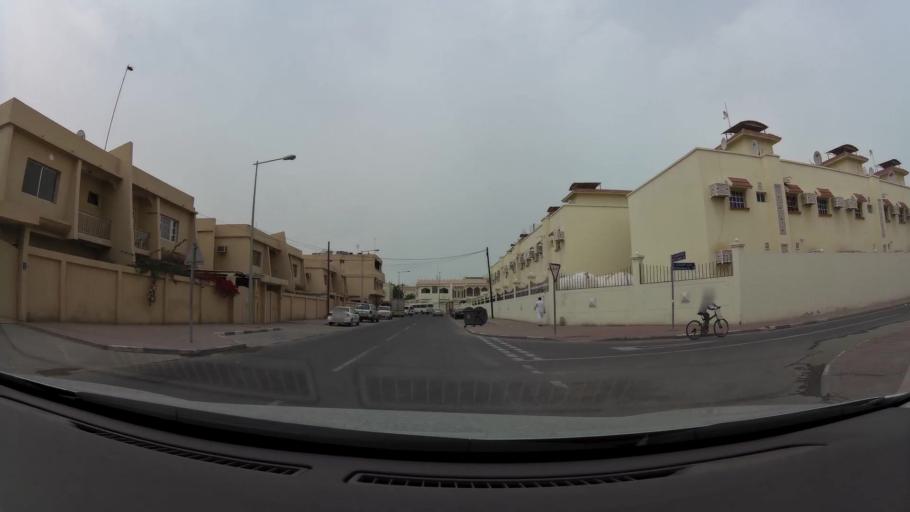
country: QA
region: Baladiyat ad Dawhah
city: Doha
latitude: 25.2478
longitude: 51.5625
